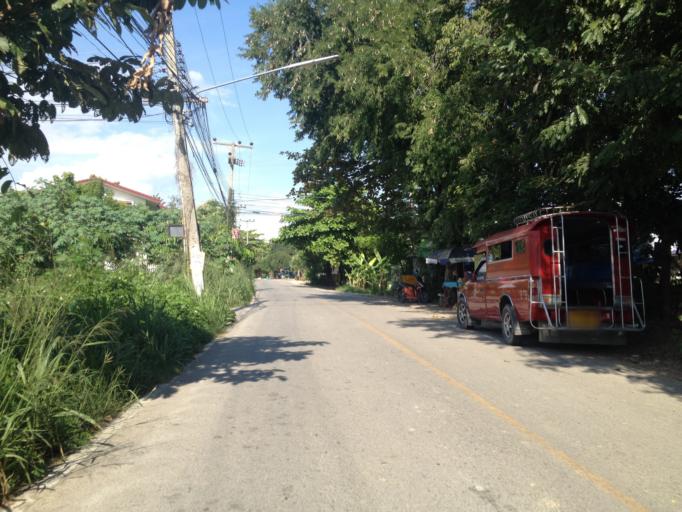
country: TH
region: Chiang Mai
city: Chiang Mai
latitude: 18.7492
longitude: 98.9851
